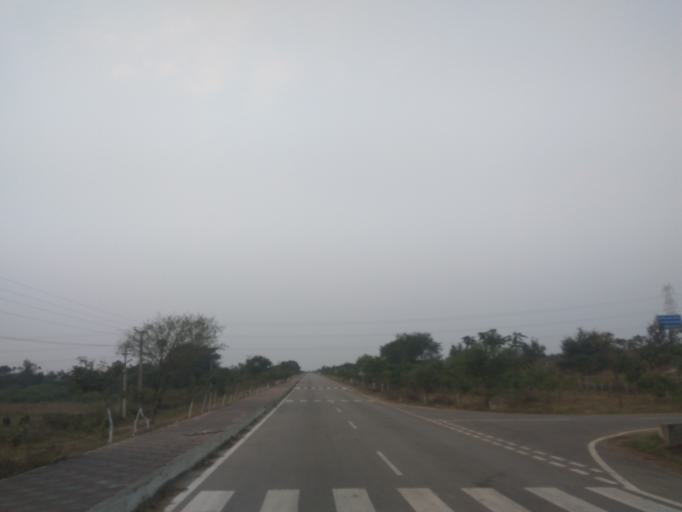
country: IN
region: Telangana
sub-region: Rangareddi
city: Secunderabad
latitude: 17.5483
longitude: 78.6292
